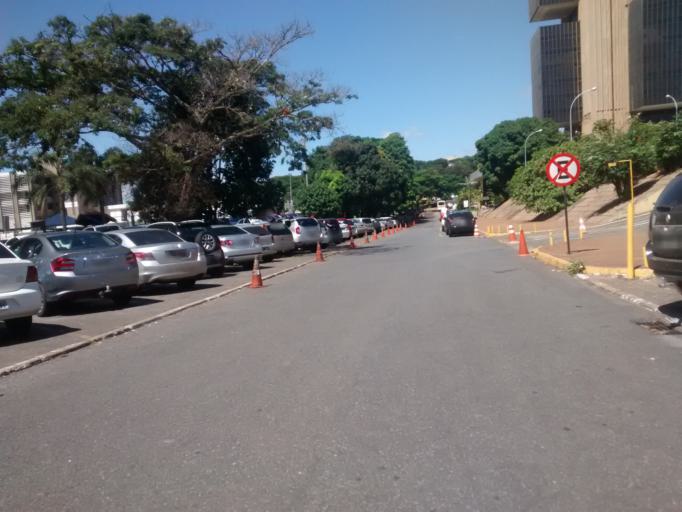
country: BR
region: Federal District
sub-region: Brasilia
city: Brasilia
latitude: -15.8021
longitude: -47.8840
